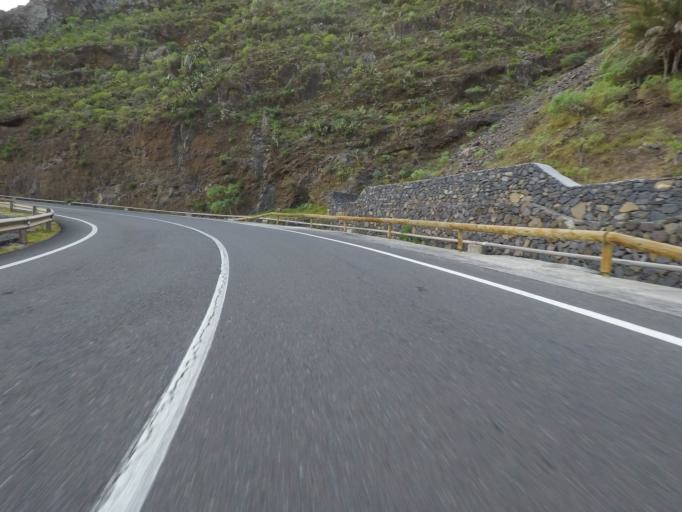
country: ES
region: Canary Islands
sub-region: Provincia de Santa Cruz de Tenerife
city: San Sebastian de la Gomera
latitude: 28.1235
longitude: -17.1489
